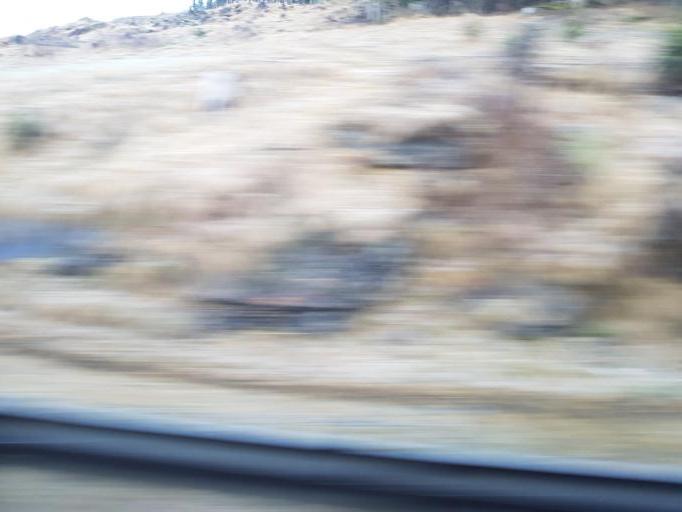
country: NO
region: Sor-Trondelag
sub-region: Midtre Gauldal
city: Storen
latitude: 62.9987
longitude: 10.2412
